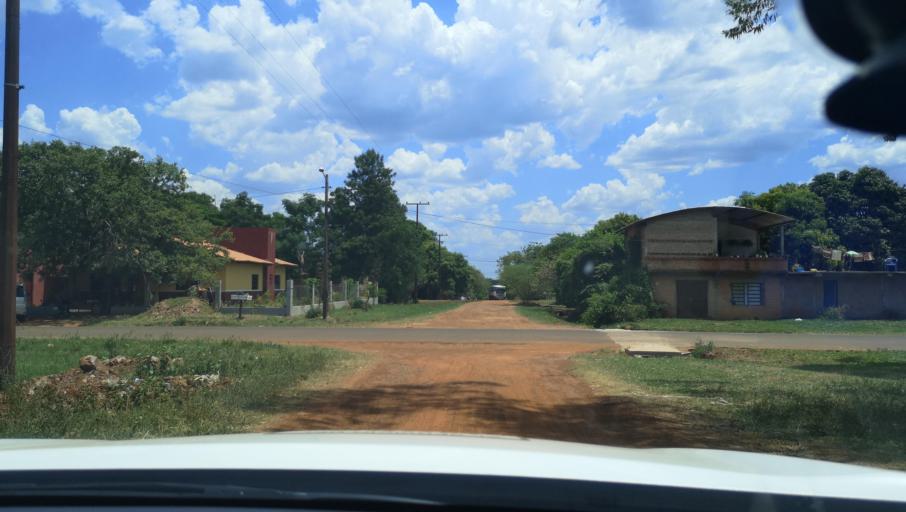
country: PY
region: Itapua
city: Carmen del Parana
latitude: -27.1698
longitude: -56.2396
